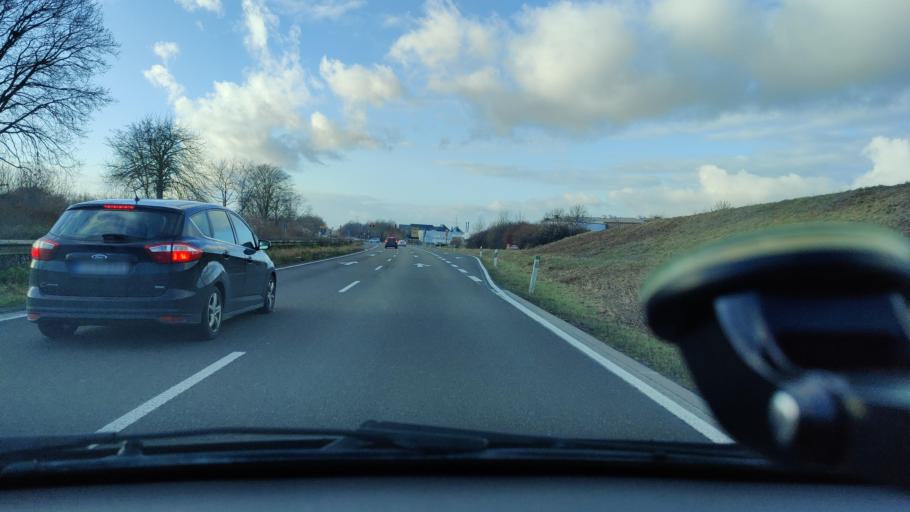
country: DE
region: North Rhine-Westphalia
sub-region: Regierungsbezirk Koln
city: Dueren
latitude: 50.8290
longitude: 6.4733
